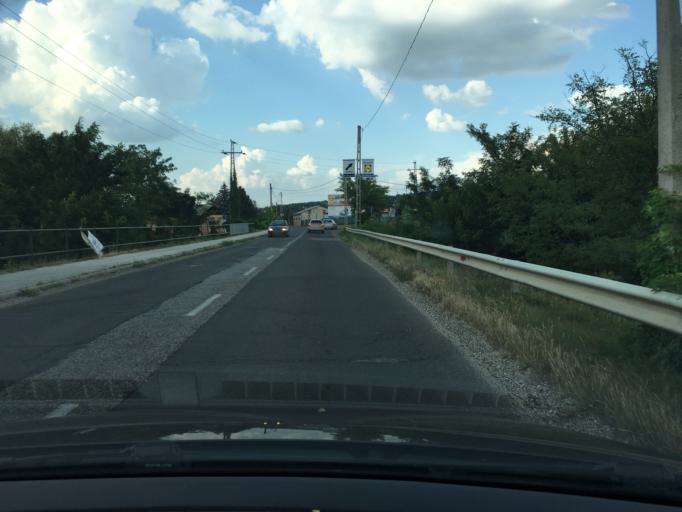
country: HU
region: Pest
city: Veresegyhaz
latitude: 47.6373
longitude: 19.3024
